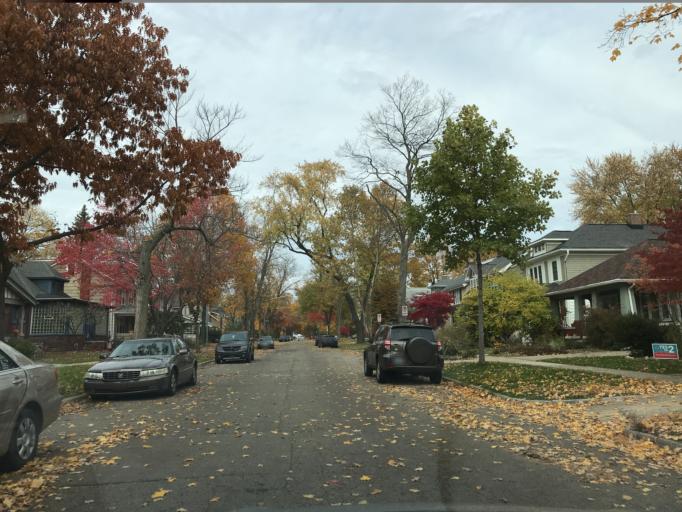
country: US
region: Michigan
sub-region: Washtenaw County
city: Ann Arbor
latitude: 42.2670
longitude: -83.7314
